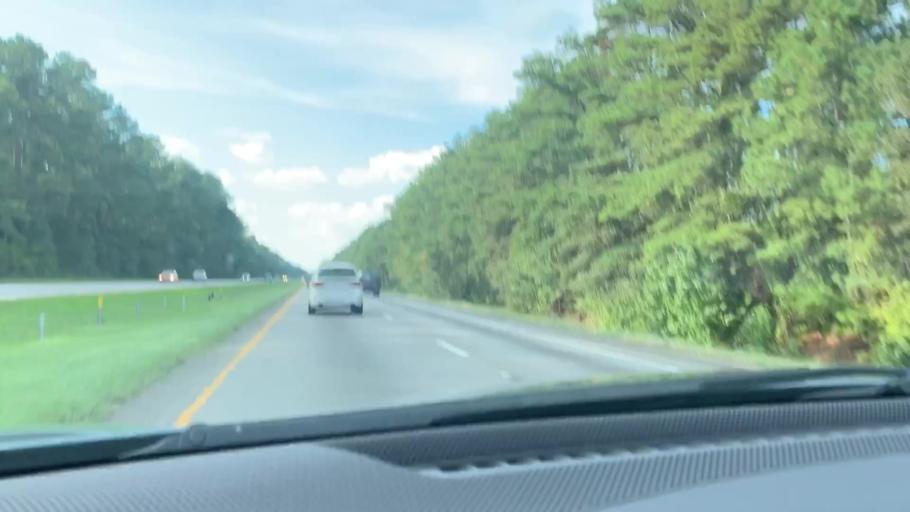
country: US
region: South Carolina
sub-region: Orangeburg County
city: Brookdale
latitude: 33.5061
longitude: -80.7758
